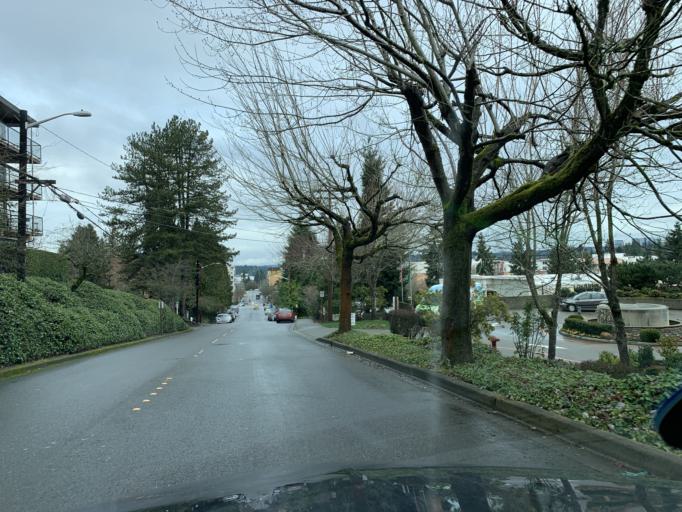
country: US
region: Washington
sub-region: King County
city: Mercer Island
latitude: 47.5849
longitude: -122.2377
